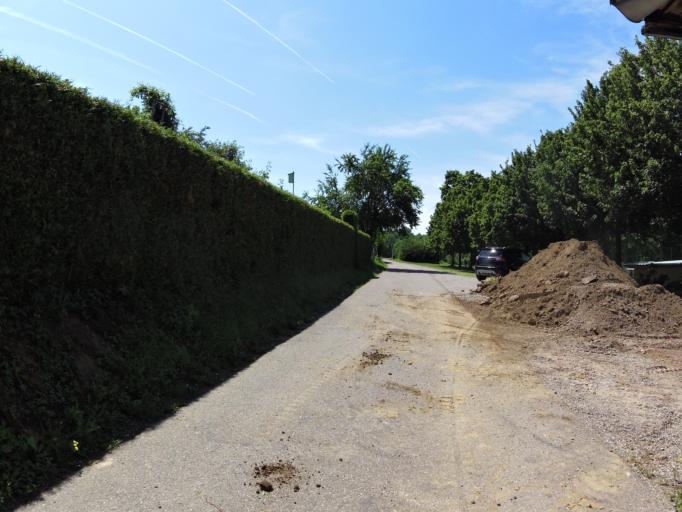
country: DE
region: Baden-Wuerttemberg
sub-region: Freiburg Region
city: Lahr
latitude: 48.3298
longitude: 7.8624
